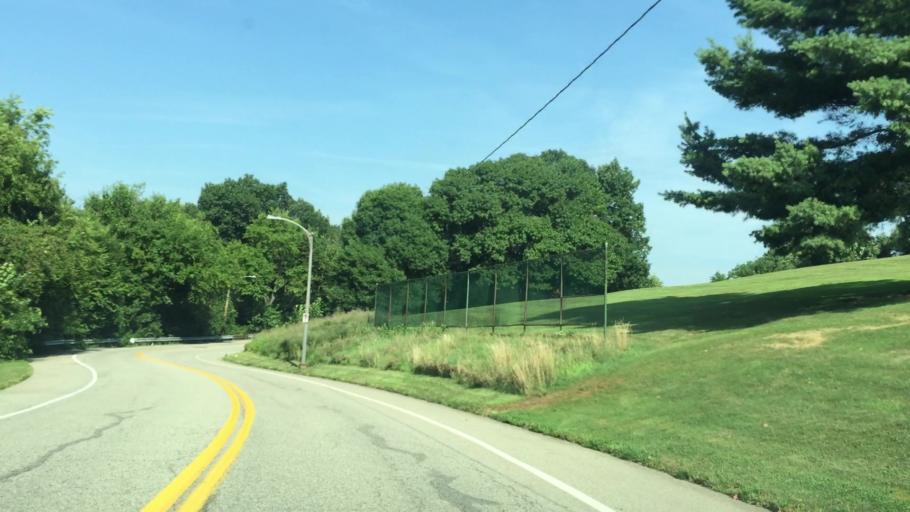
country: US
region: Pennsylvania
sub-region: Allegheny County
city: Bloomfield
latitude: 40.4387
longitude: -79.9395
